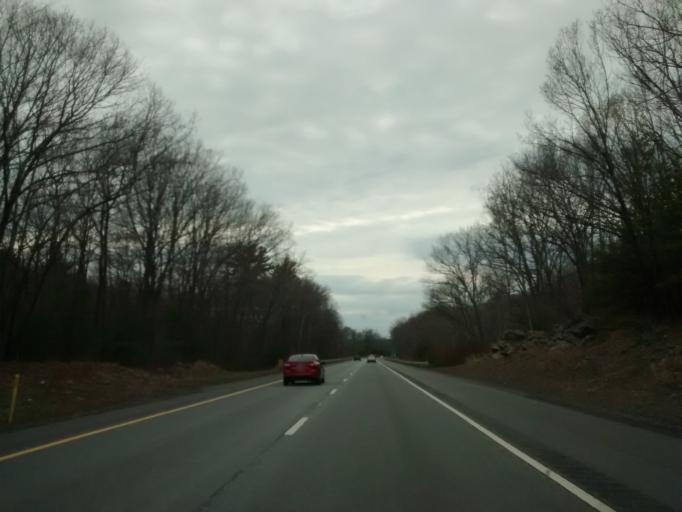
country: US
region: Massachusetts
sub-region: Worcester County
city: East Douglas
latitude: 42.0723
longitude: -71.6757
